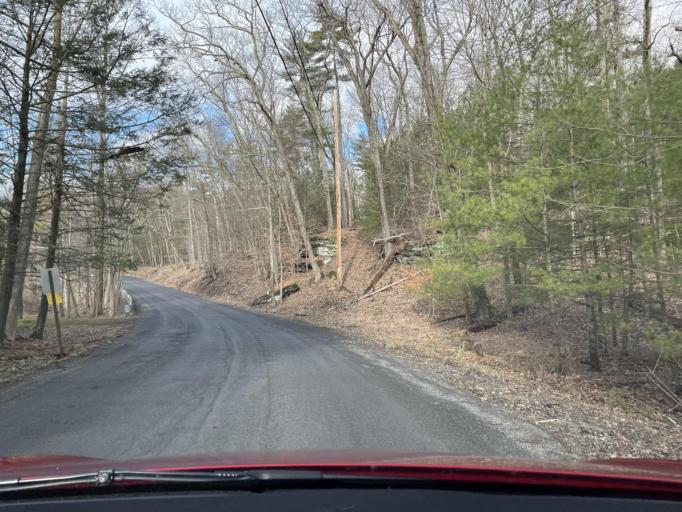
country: US
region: New York
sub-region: Ulster County
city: Woodstock
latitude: 42.0504
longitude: -74.1281
